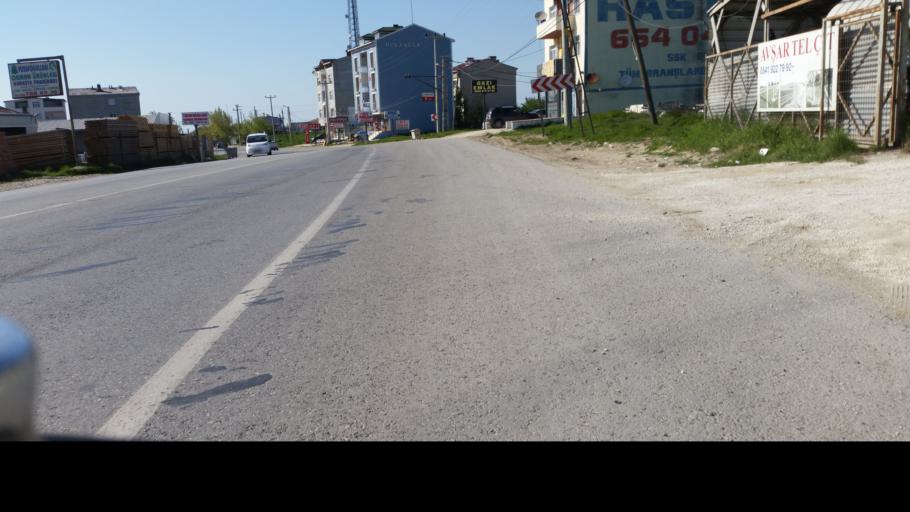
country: TR
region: Tekirdag
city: Cerkezkoey
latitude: 41.3556
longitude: 27.9545
